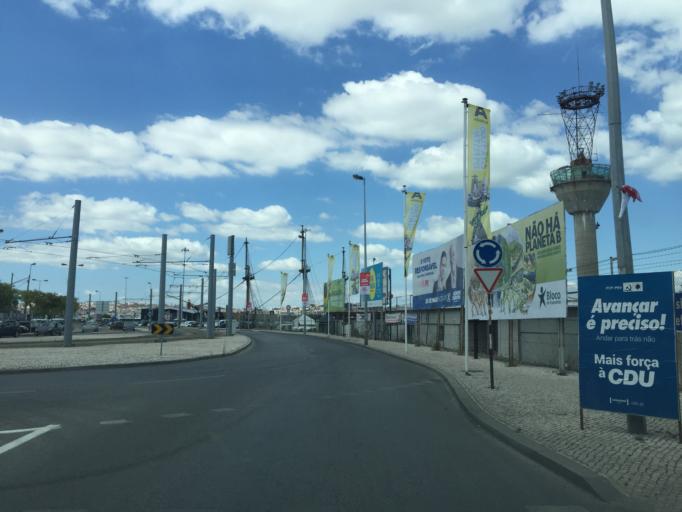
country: PT
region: Setubal
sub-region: Almada
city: Cacilhas
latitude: 38.6847
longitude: -9.1468
